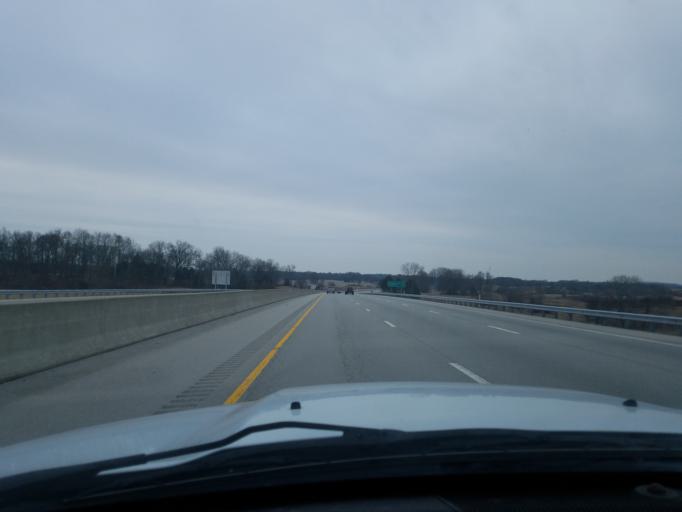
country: US
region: Kentucky
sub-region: Barren County
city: Cave City
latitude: 37.0888
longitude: -86.0619
